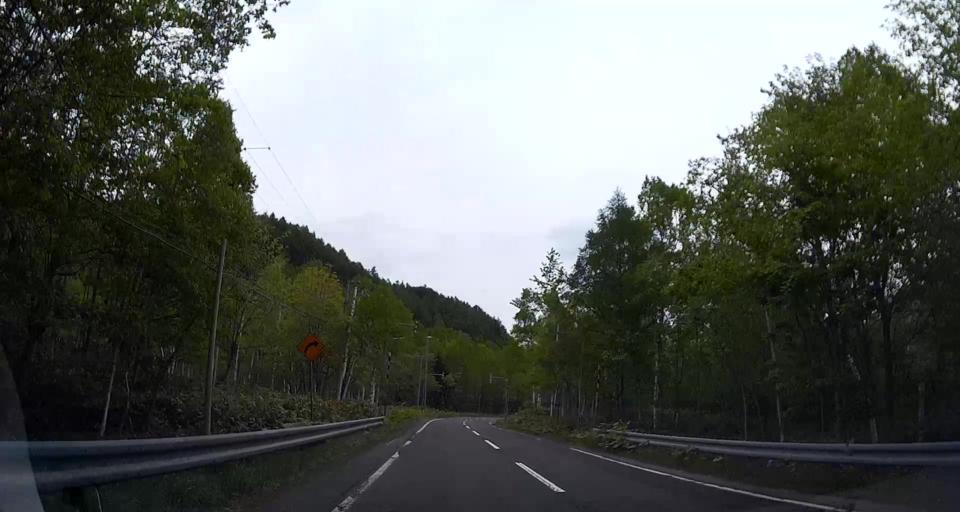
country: JP
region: Hokkaido
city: Shiraoi
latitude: 42.6869
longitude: 141.1028
